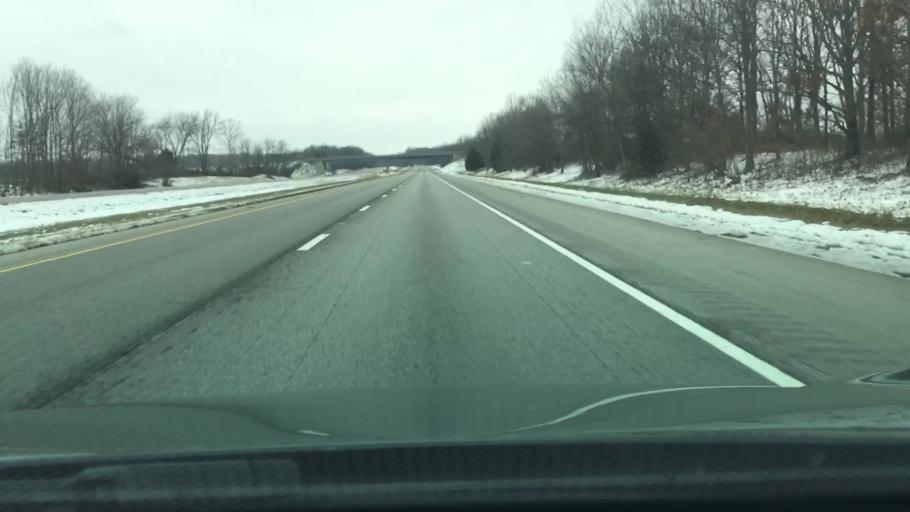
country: US
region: Illinois
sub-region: Jefferson County
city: Mount Vernon
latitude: 38.3517
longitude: -88.9884
